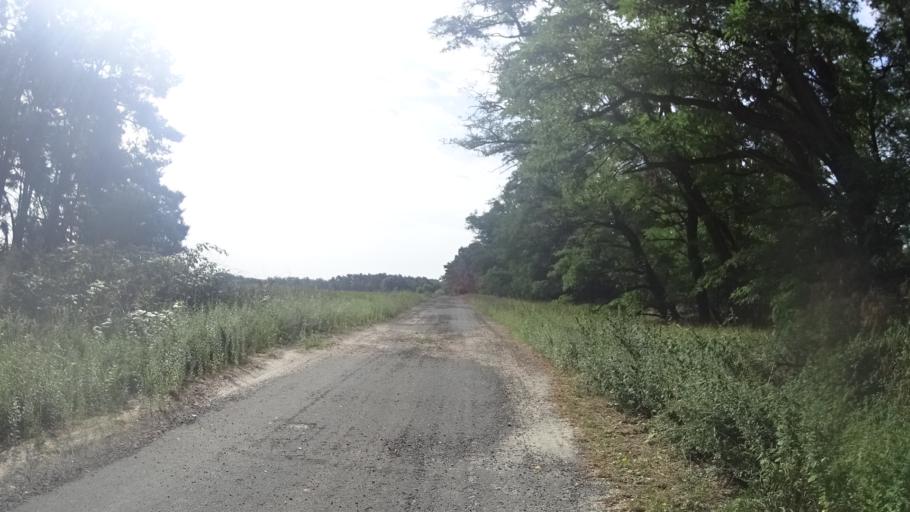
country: DE
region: Brandenburg
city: Brandenburg an der Havel
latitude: 52.3734
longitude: 12.6227
